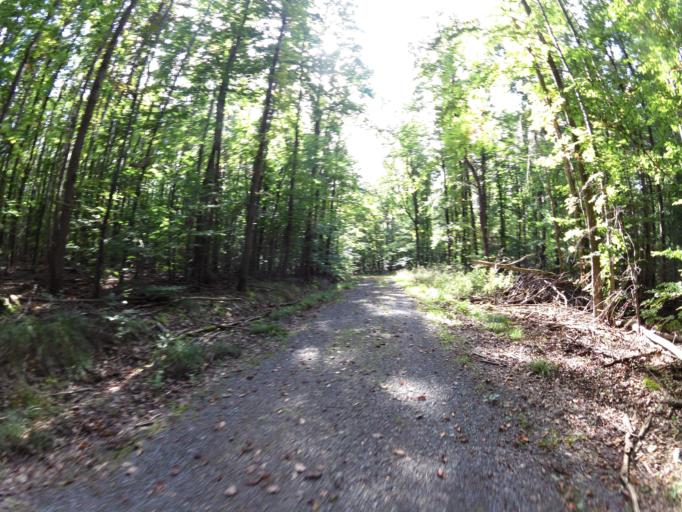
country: DE
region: Bavaria
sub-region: Regierungsbezirk Unterfranken
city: Waldbrunn
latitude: 49.7410
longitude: 9.8168
